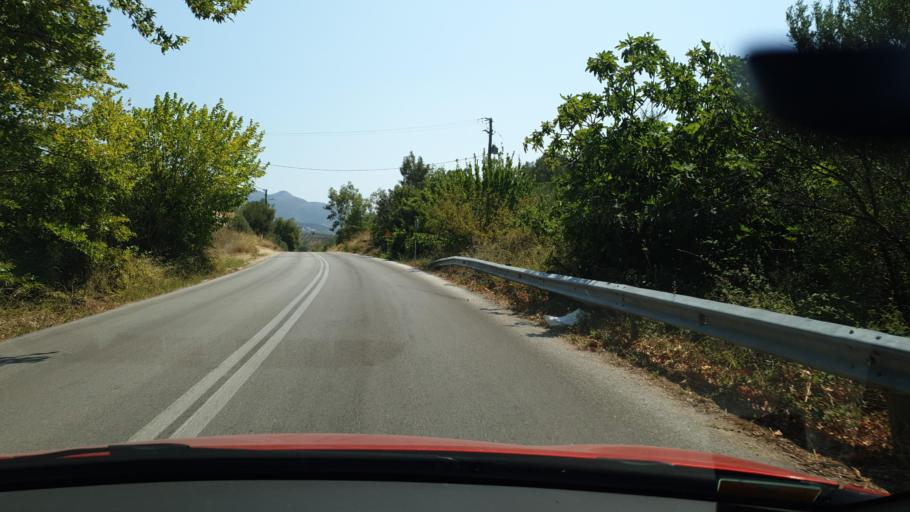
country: GR
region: Central Greece
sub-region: Nomos Evvoias
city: Oxilithos
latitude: 38.5216
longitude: 24.0944
